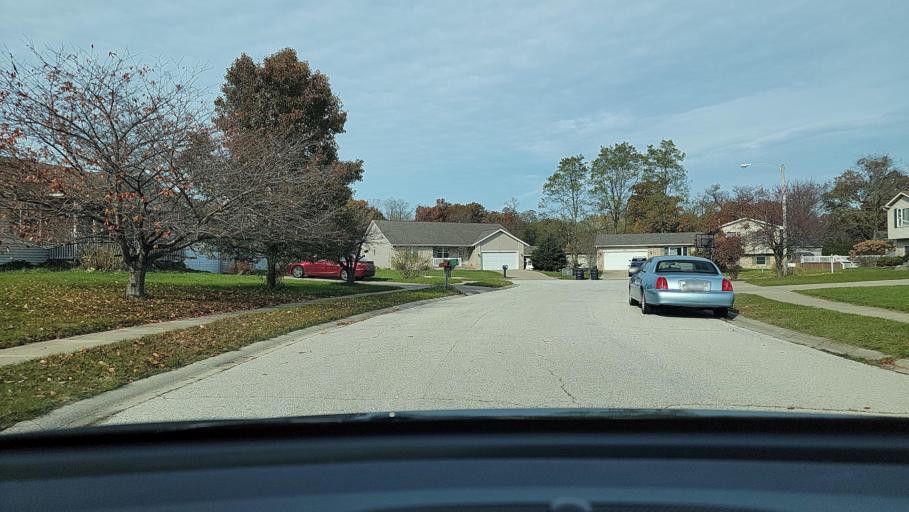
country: US
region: Indiana
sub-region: Lake County
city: Lake Station
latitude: 41.5820
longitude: -87.2156
